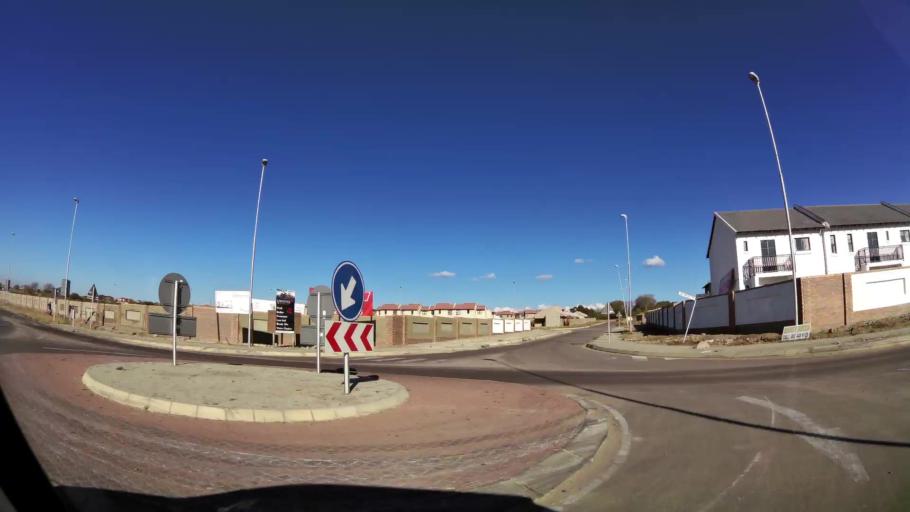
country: ZA
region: Limpopo
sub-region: Capricorn District Municipality
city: Polokwane
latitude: -23.8788
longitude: 29.4742
